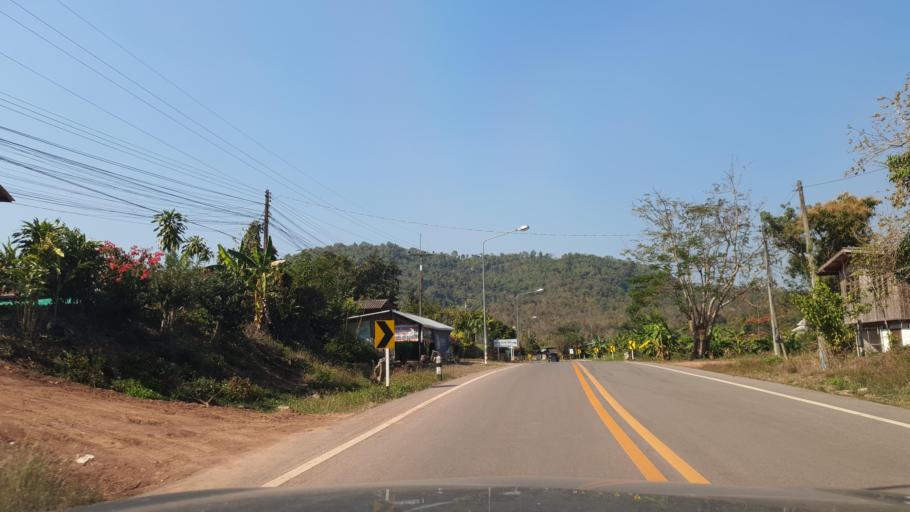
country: TH
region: Chiang Rai
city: Mae Lao
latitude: 19.8358
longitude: 99.6815
